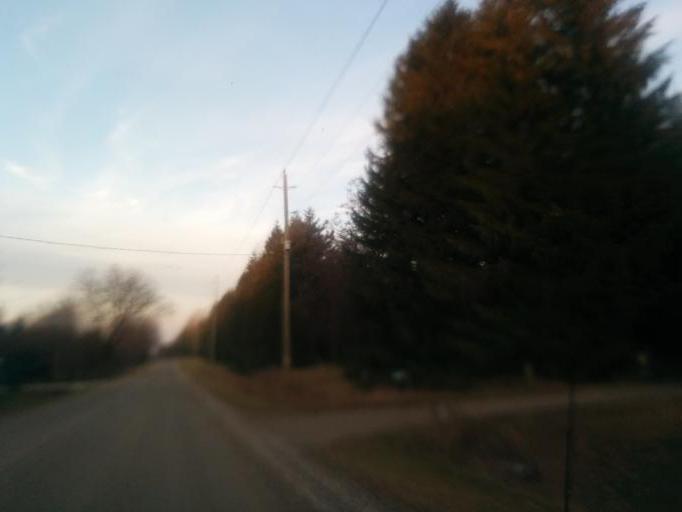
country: CA
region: Ontario
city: Orangeville
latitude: 43.9629
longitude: -79.9791
